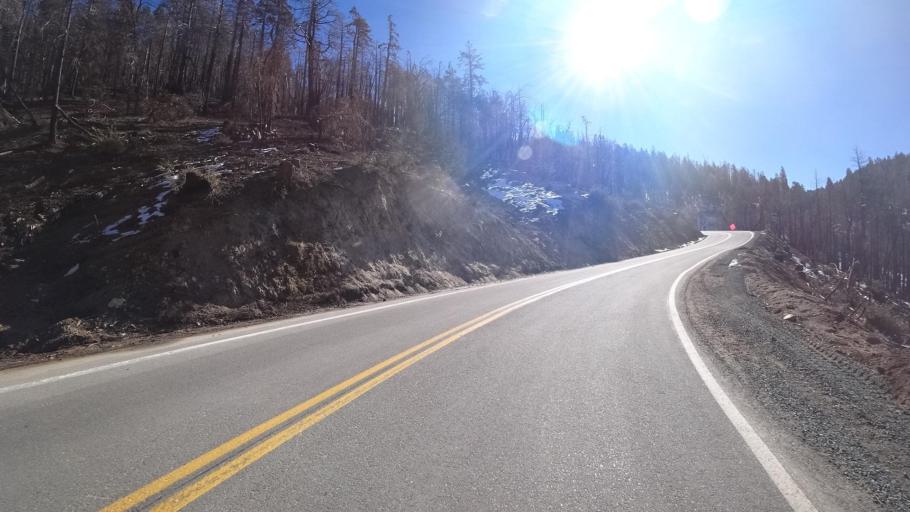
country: US
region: California
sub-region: Kern County
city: Alta Sierra
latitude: 35.7463
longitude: -118.5555
